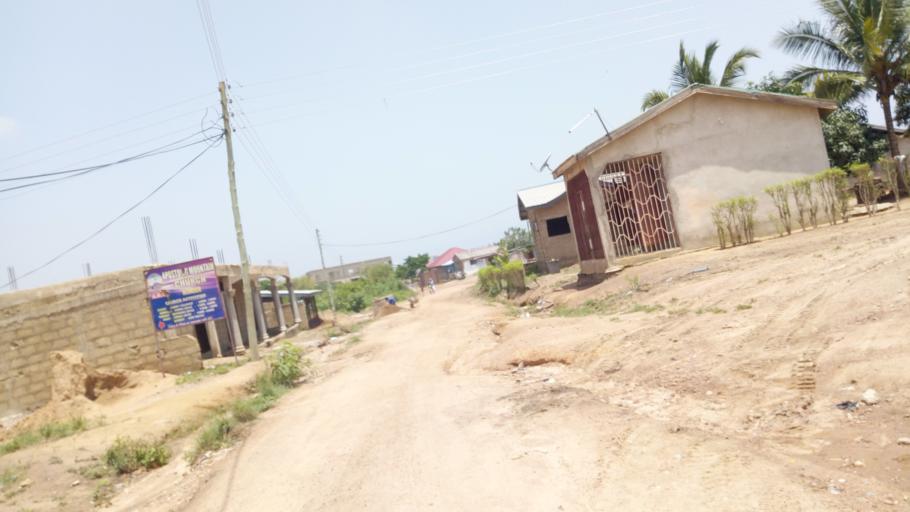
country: GH
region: Central
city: Kasoa
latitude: 5.5037
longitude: -0.4488
